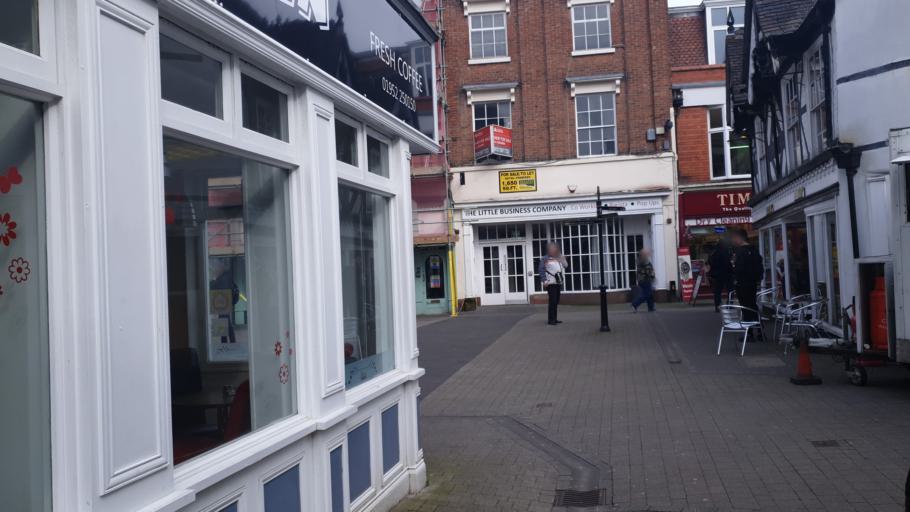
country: GB
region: England
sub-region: Telford and Wrekin
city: Wellington
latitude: 52.7008
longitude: -2.5187
